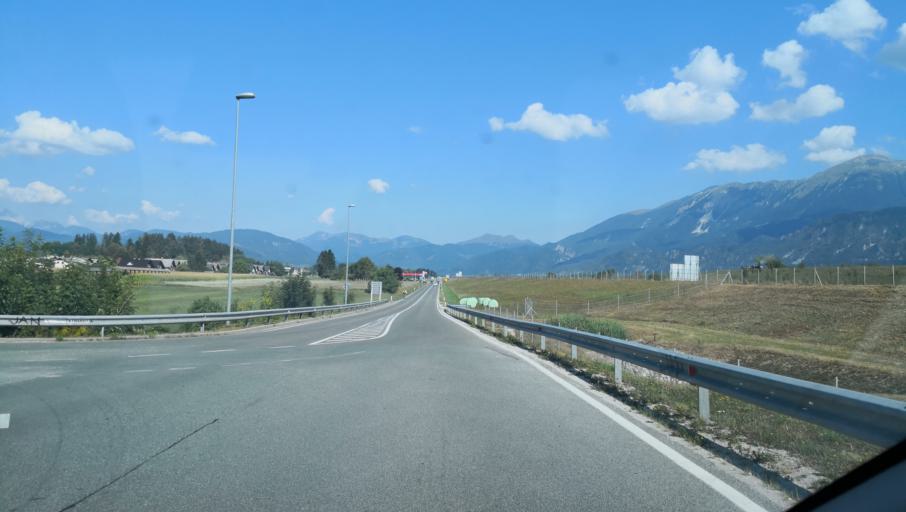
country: SI
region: Radovljica
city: Radovljica
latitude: 46.3428
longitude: 14.1855
